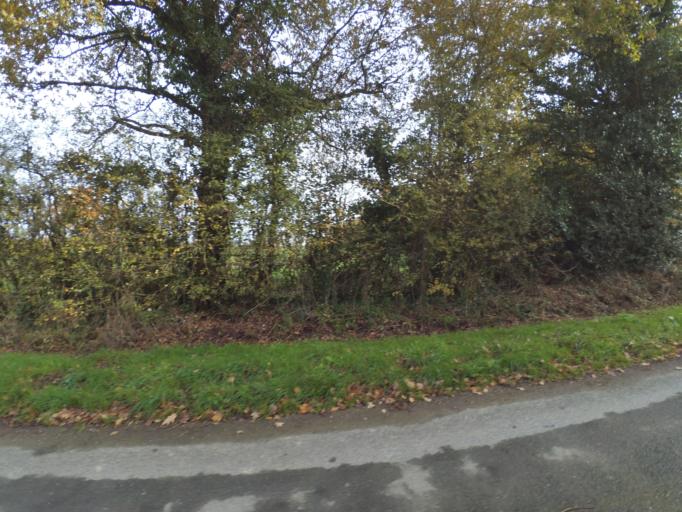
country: FR
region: Pays de la Loire
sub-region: Departement de la Loire-Atlantique
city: La Planche
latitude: 47.0198
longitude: -1.4023
